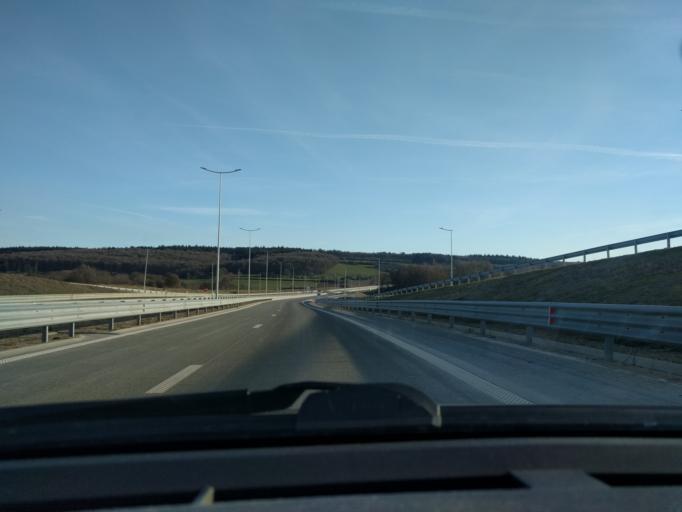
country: BE
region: Wallonia
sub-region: Province de Namur
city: Couvin
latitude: 50.0537
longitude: 4.5087
